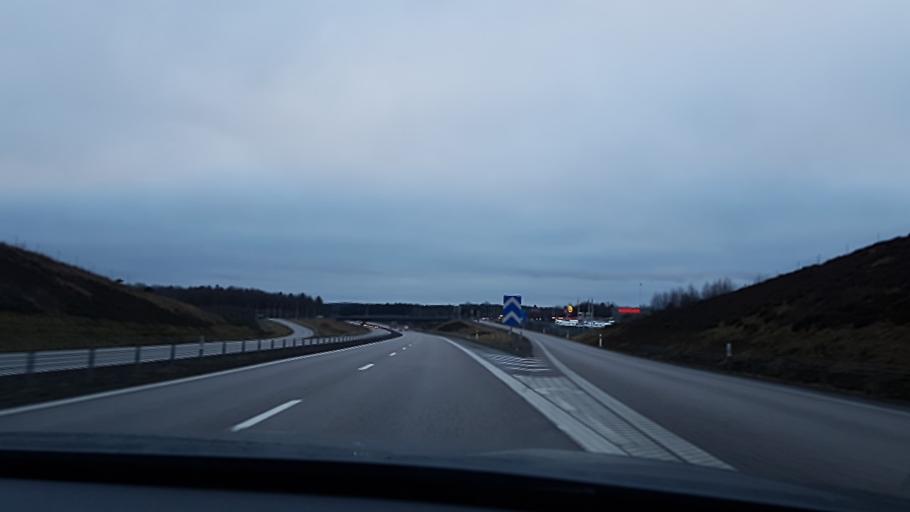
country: SE
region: Skane
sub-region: Orkelljunga Kommun
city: OErkelljunga
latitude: 56.2870
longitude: 13.3461
